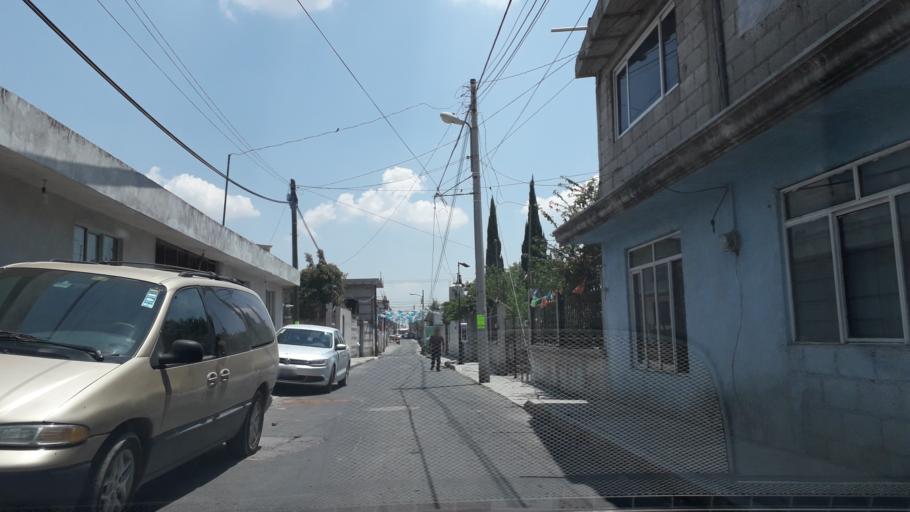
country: MX
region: Puebla
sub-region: Puebla
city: Santa Maria Xonacatepec
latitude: 19.0893
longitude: -98.1031
